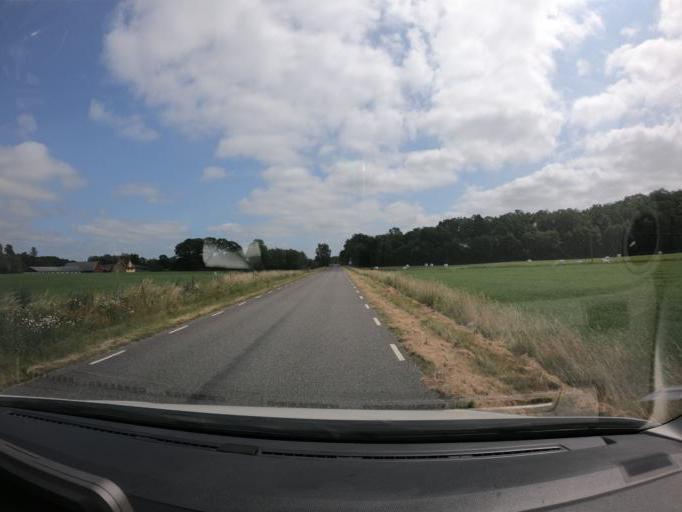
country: SE
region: Skane
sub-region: Hassleholms Kommun
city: Sosdala
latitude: 56.0457
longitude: 13.6612
